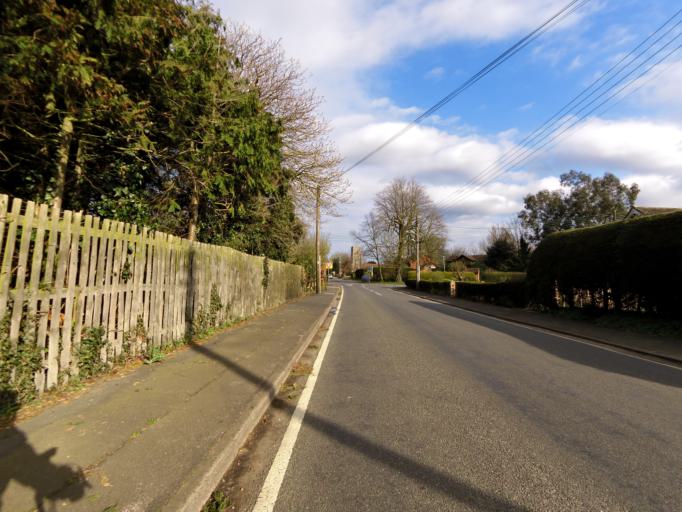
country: GB
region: England
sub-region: Suffolk
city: Ipswich
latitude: 52.0849
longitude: 1.1707
